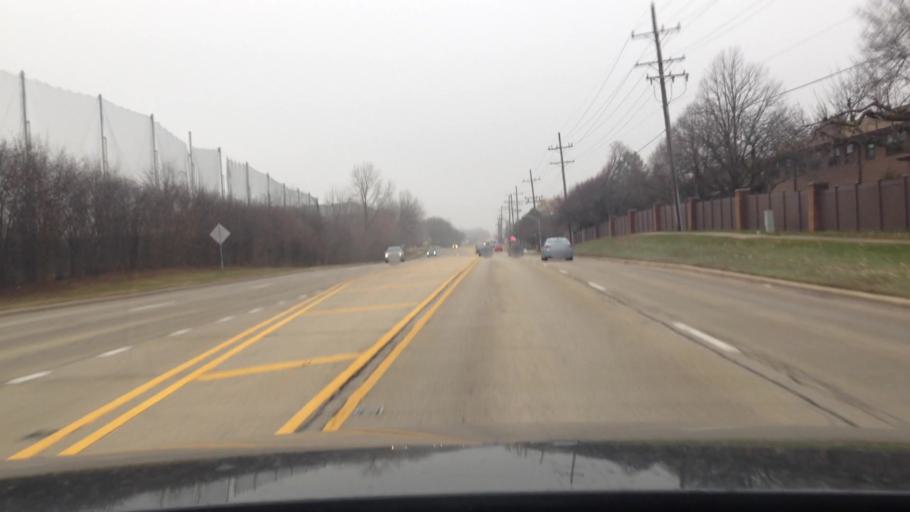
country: US
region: Illinois
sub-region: DuPage County
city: Westmont
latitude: 41.8200
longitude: -87.9764
